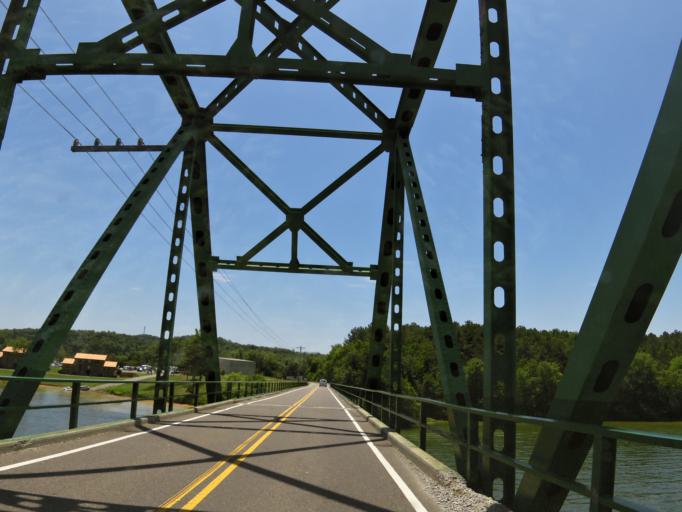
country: US
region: Tennessee
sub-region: Jefferson County
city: Dandridge
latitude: 36.0115
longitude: -83.4125
